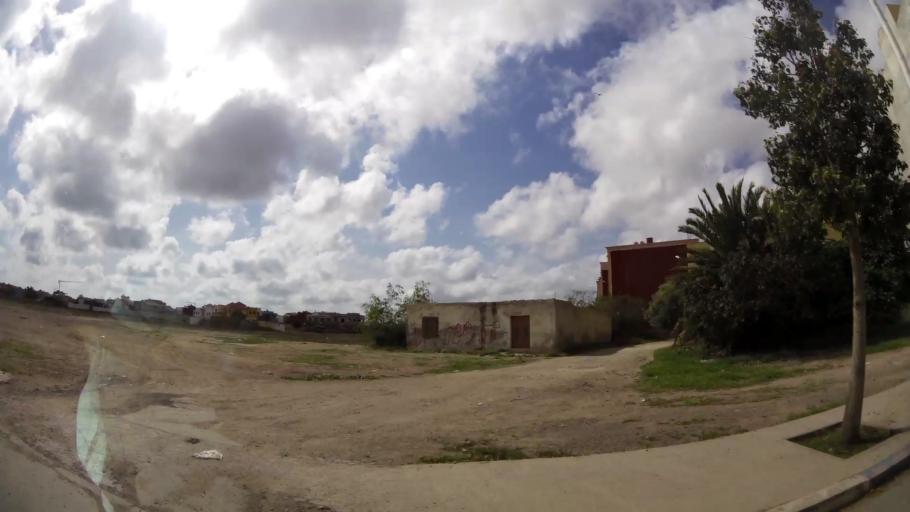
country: MA
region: Oriental
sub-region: Nador
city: Nador
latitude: 35.1635
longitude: -2.9211
